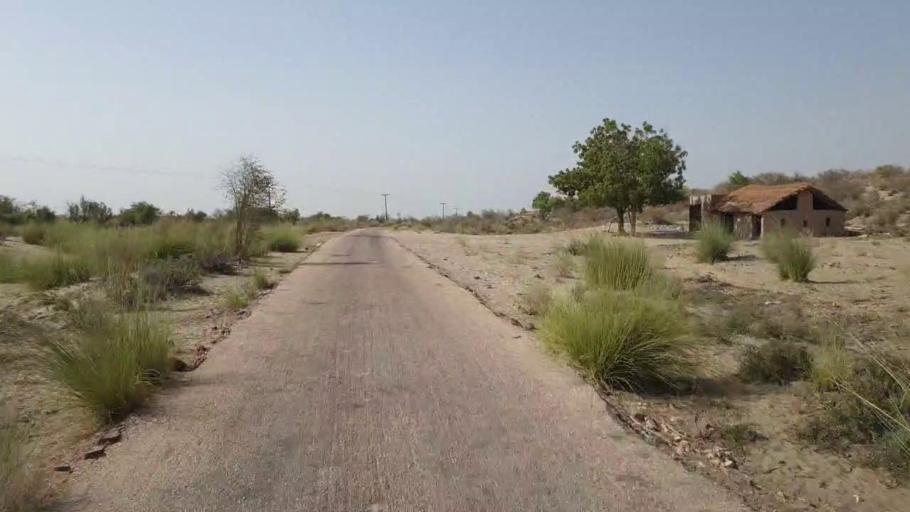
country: PK
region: Sindh
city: Jam Sahib
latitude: 26.5779
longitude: 68.9210
